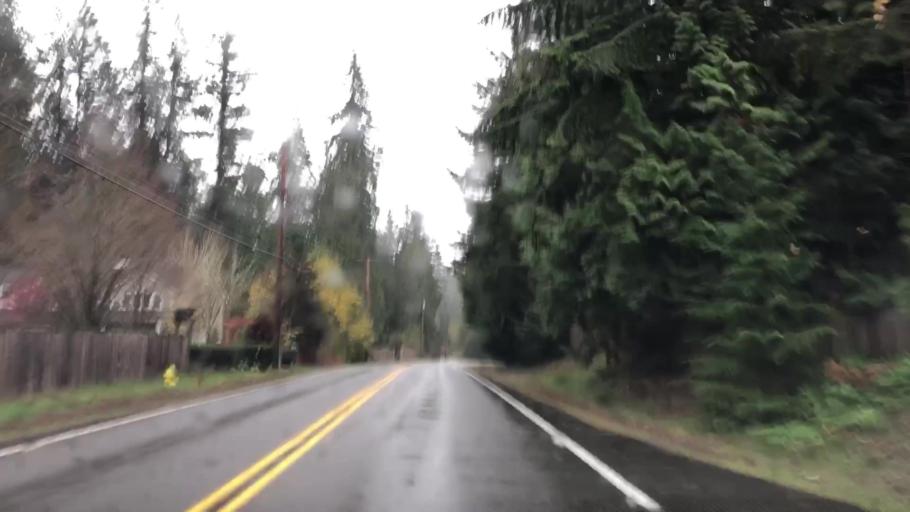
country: US
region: Washington
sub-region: King County
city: Cottage Lake
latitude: 47.7585
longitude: -122.1111
